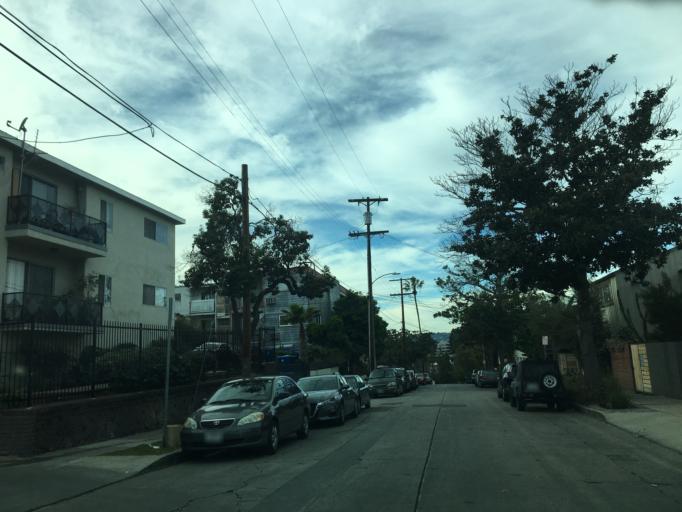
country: US
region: California
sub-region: Los Angeles County
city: Echo Park
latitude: 34.0632
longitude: -118.2772
